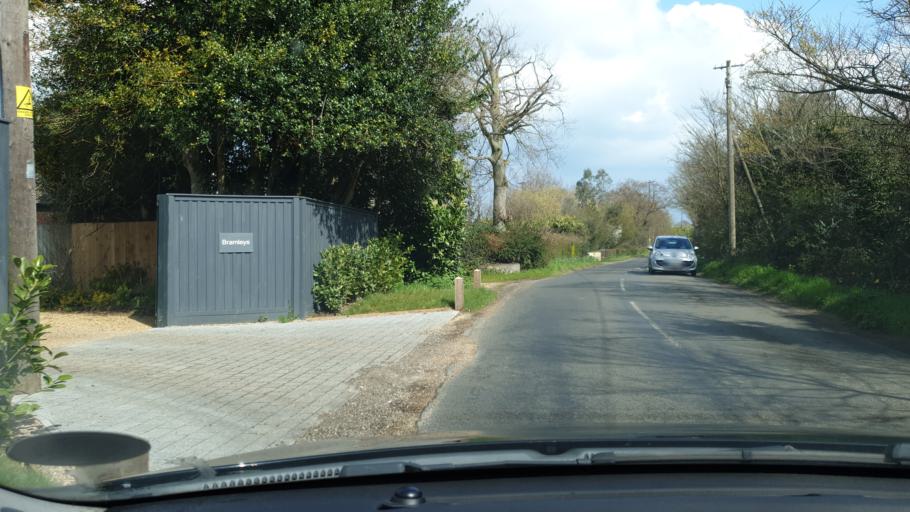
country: GB
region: England
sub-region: Essex
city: Great Bentley
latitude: 51.8652
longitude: 1.1004
